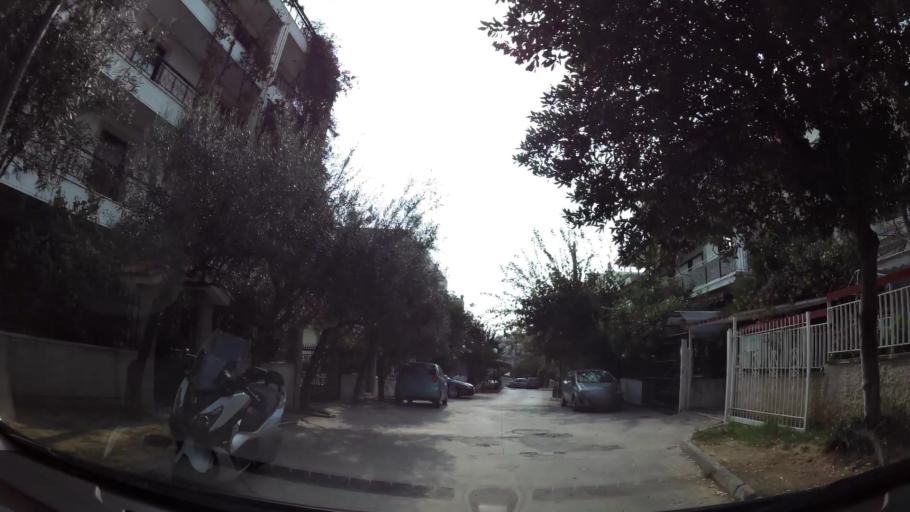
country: GR
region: Attica
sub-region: Nomarchia Athinas
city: Irakleio
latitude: 38.0540
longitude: 23.7672
